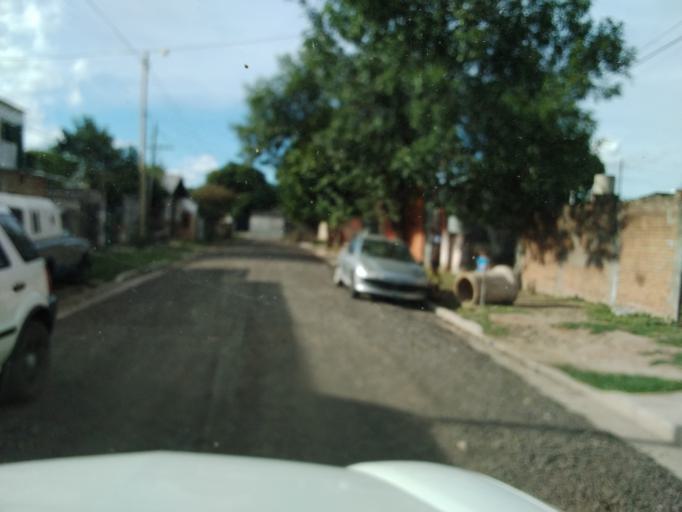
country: AR
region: Corrientes
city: Corrientes
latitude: -27.4897
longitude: -58.8412
